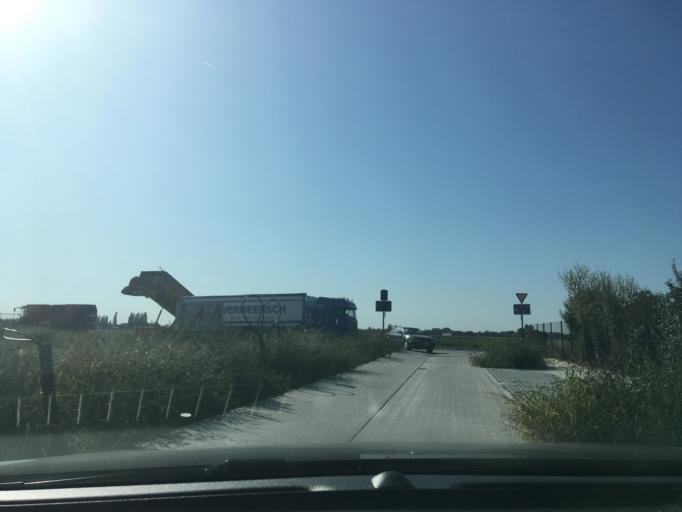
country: BE
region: Flanders
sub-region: Provincie West-Vlaanderen
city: Roeselare
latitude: 50.9111
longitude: 3.1593
